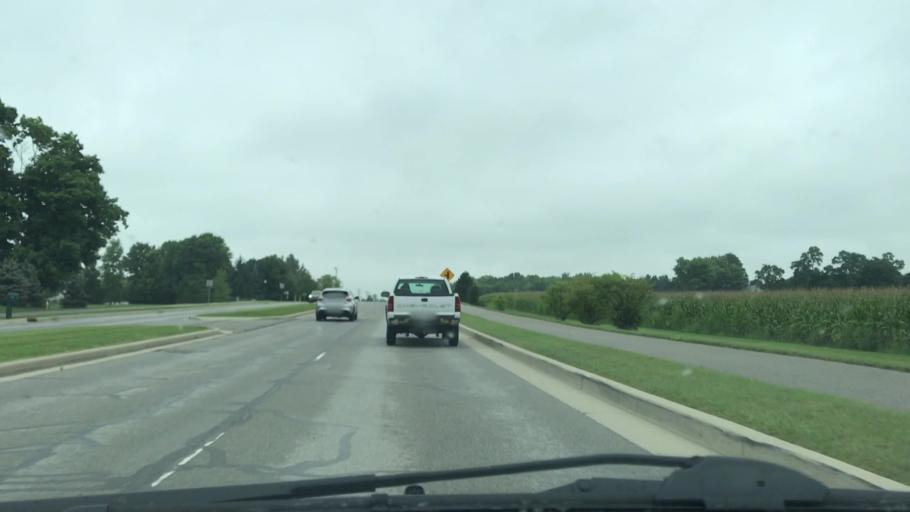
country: US
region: Indiana
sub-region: Hamilton County
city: Westfield
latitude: 40.0354
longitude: -86.0706
